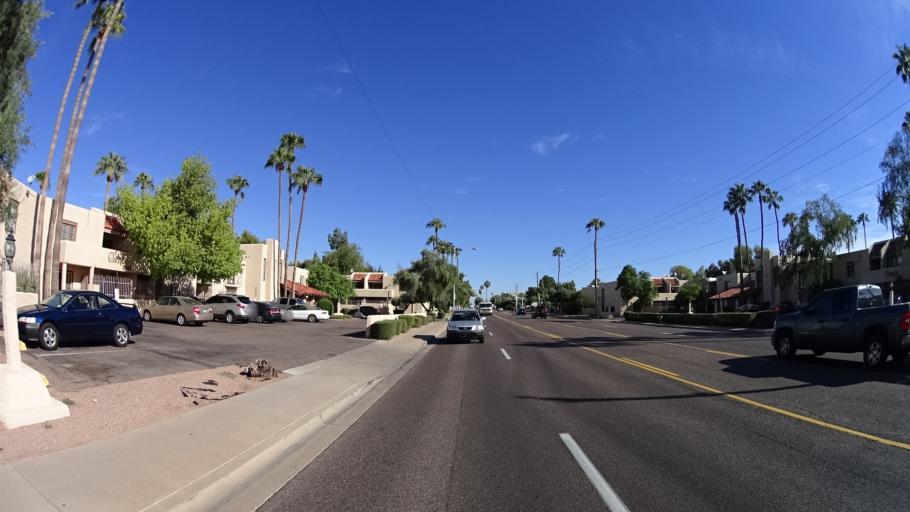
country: US
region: Arizona
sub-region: Maricopa County
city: Scottsdale
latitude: 33.4864
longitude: -111.9348
